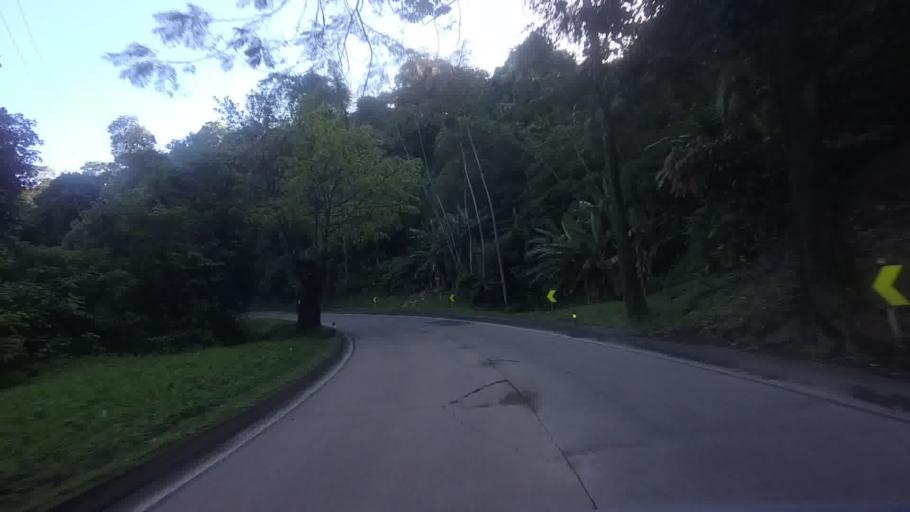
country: BR
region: Rio de Janeiro
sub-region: Petropolis
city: Petropolis
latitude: -22.5696
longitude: -43.2508
